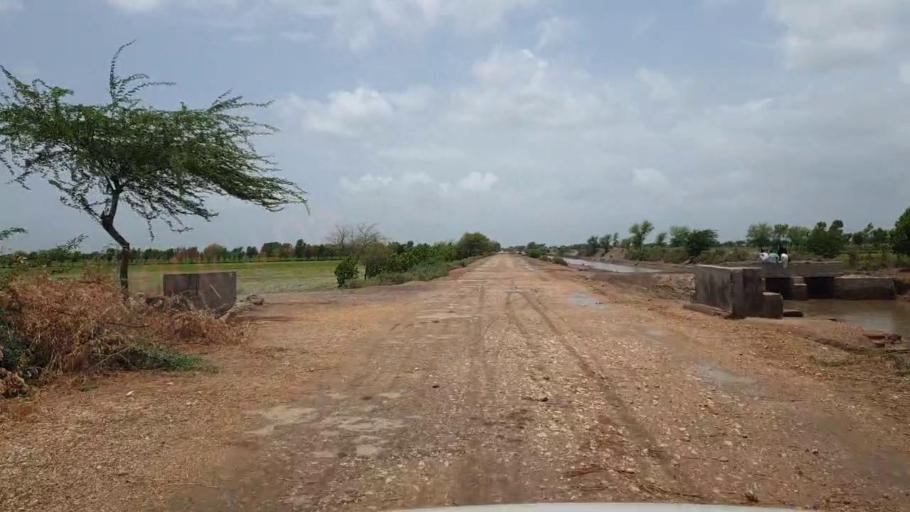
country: PK
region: Sindh
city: Kario
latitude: 24.7115
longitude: 68.5961
